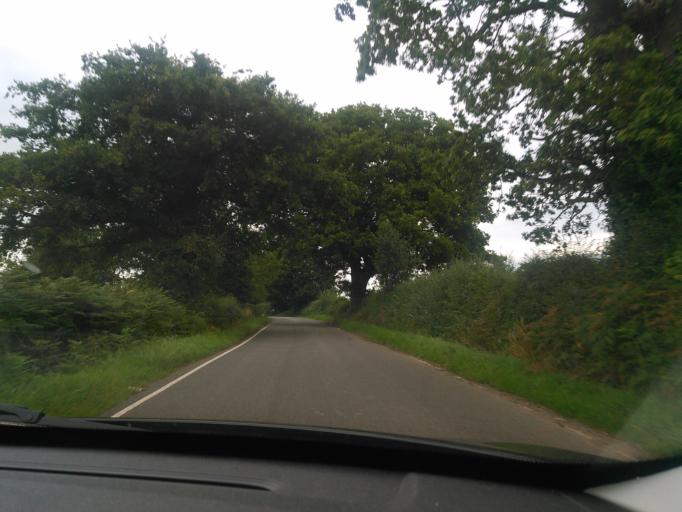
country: GB
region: England
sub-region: Shropshire
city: Prees
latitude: 52.8651
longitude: -2.6650
